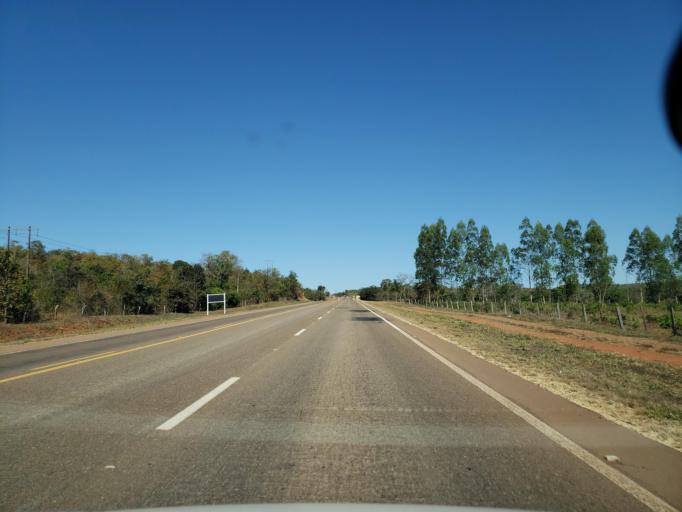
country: BR
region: Mato Grosso
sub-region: Poxoreo
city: Poxoreo
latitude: -15.7846
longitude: -54.3729
